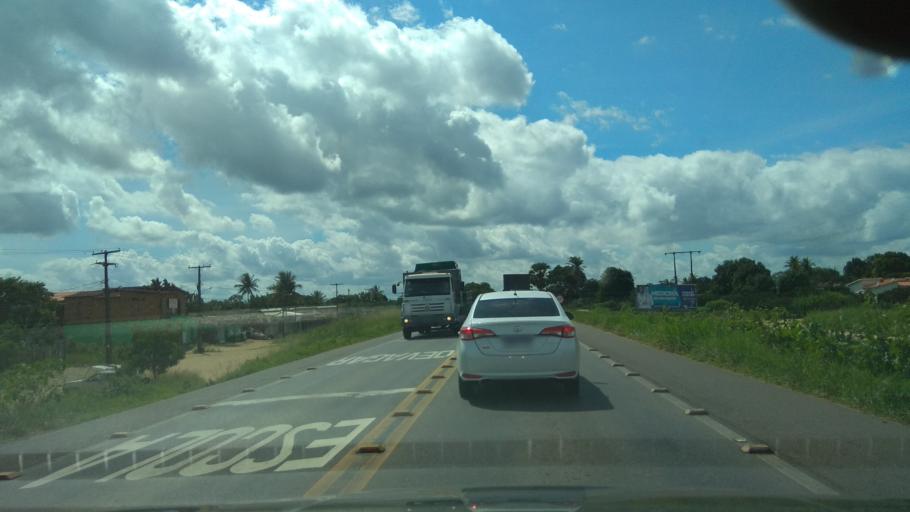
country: BR
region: Bahia
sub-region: Cruz Das Almas
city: Cruz das Almas
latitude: -12.6273
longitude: -39.0913
